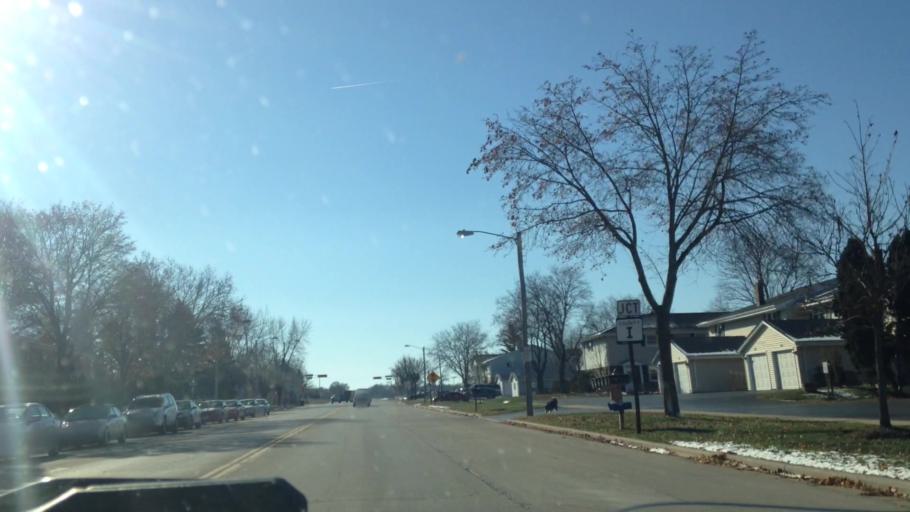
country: US
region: Wisconsin
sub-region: Washington County
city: West Bend
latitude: 43.4143
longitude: -88.1613
